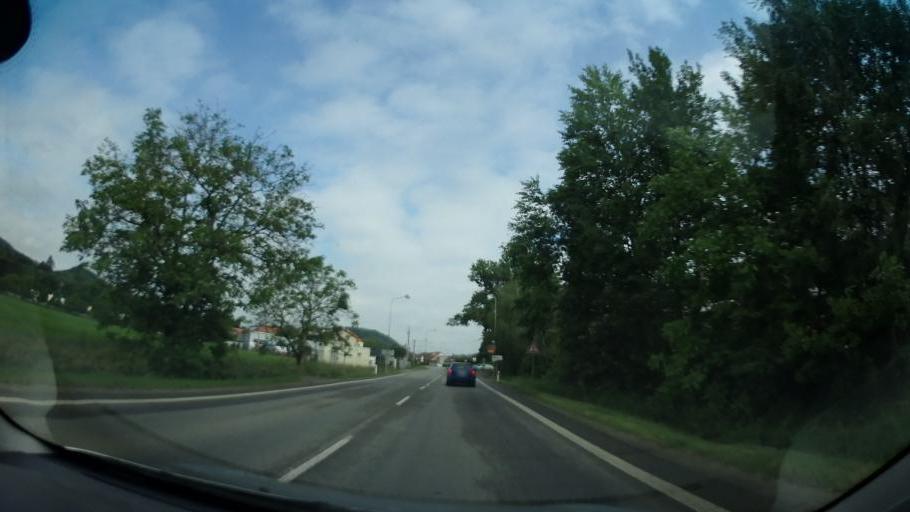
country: CZ
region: South Moravian
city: Predklasteri
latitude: 49.3505
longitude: 16.4089
